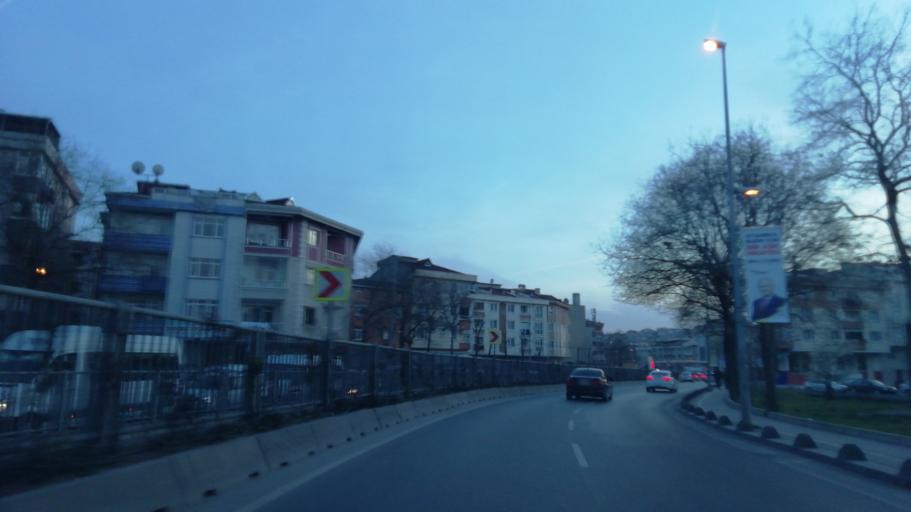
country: TR
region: Istanbul
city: Bagcilar
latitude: 41.0307
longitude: 28.8483
